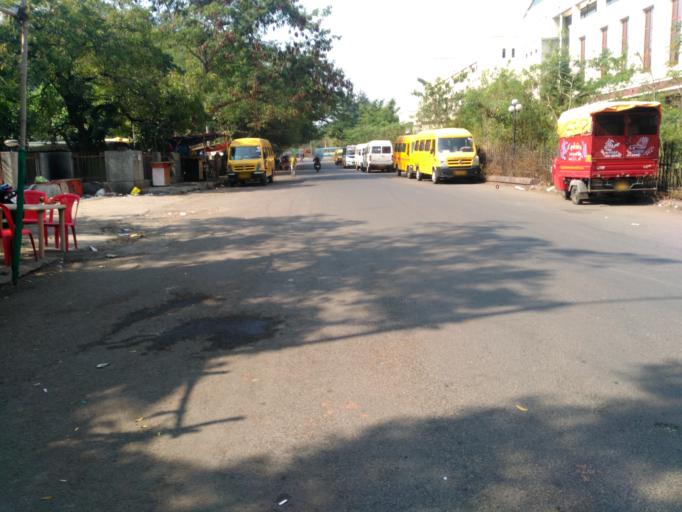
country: IN
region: Maharashtra
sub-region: Pune Division
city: Khadki
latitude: 18.5546
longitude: 73.8918
